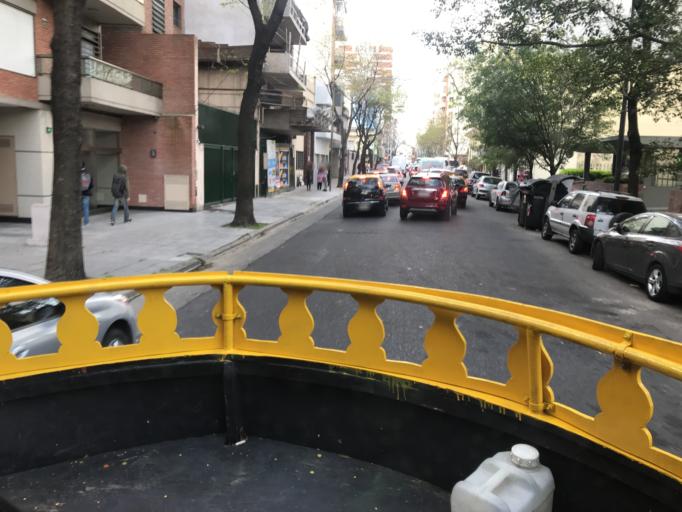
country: AR
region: Buenos Aires F.D.
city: Retiro
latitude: -34.5990
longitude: -58.4122
